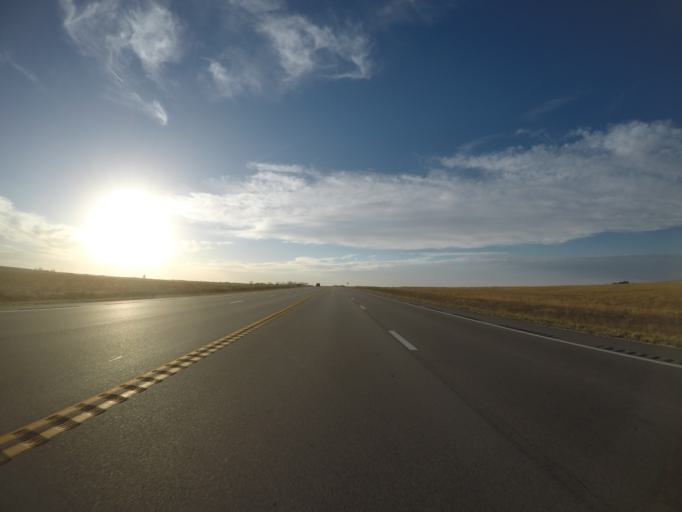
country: US
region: Kansas
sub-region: Chase County
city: Cottonwood Falls
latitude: 38.4055
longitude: -96.4122
